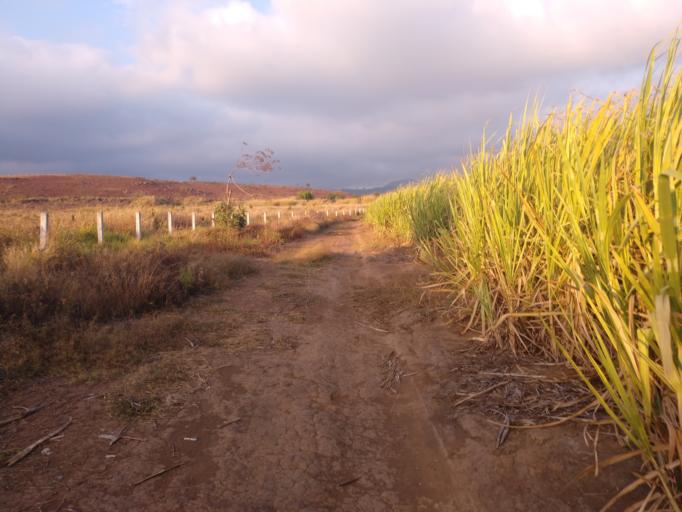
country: MX
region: Nayarit
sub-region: Tepic
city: La Corregidora
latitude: 21.4855
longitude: -104.8099
